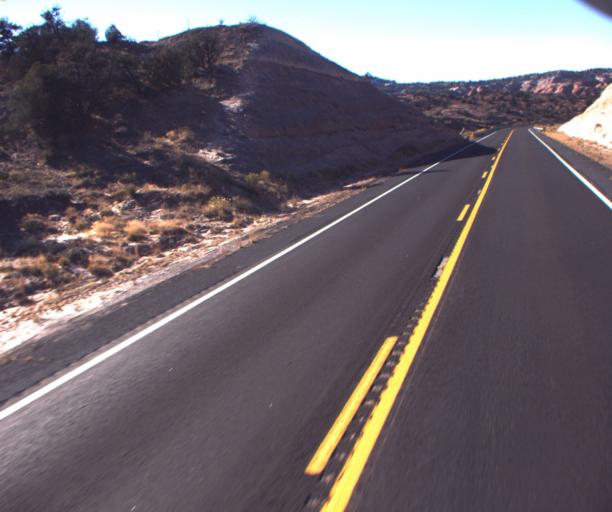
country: US
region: Arizona
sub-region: Coconino County
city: Kaibito
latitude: 36.5951
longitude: -110.9076
